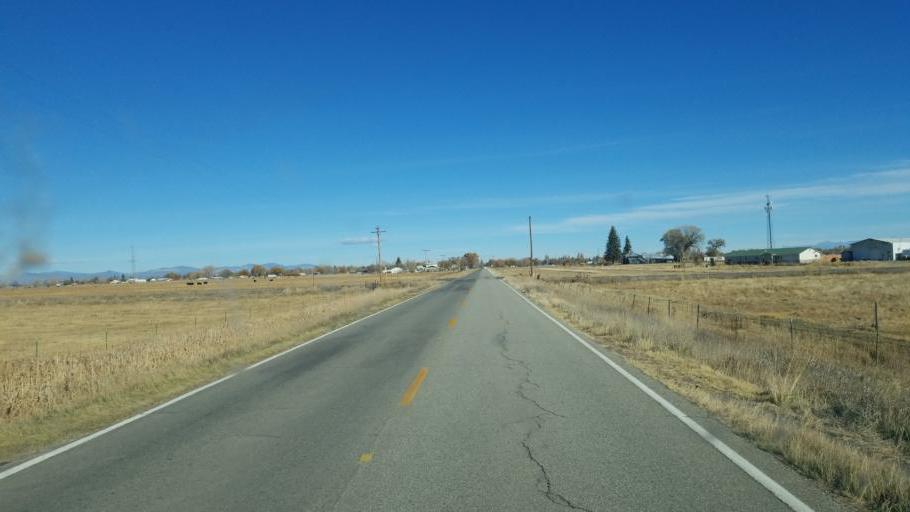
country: US
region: Colorado
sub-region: Rio Grande County
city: Monte Vista
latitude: 37.5592
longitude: -106.1495
